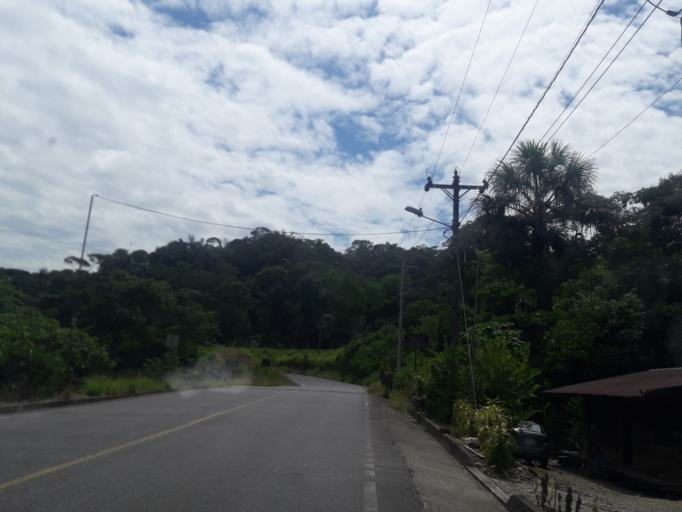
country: EC
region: Napo
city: Tena
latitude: -1.0163
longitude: -77.8610
